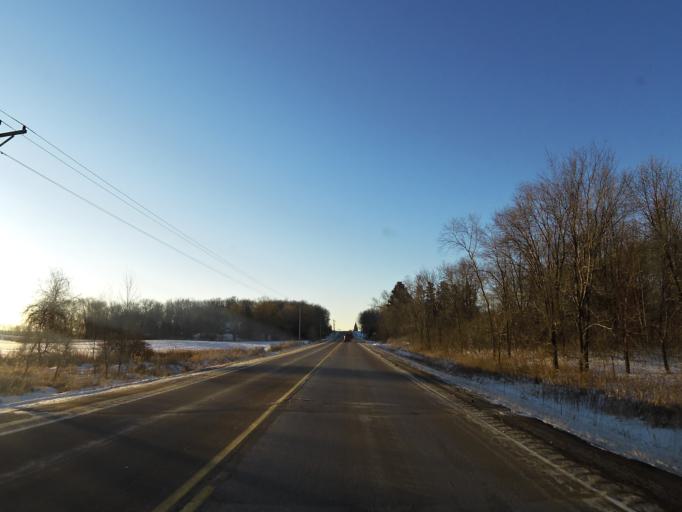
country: US
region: Minnesota
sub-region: Scott County
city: Prior Lake
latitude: 44.6854
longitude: -93.3793
